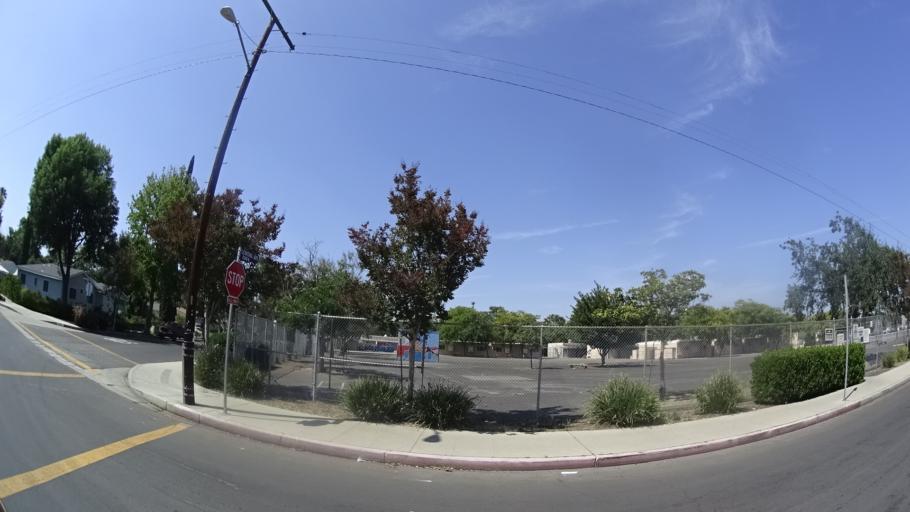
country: US
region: California
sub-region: Los Angeles County
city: Sherman Oaks
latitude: 34.1668
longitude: -118.4595
